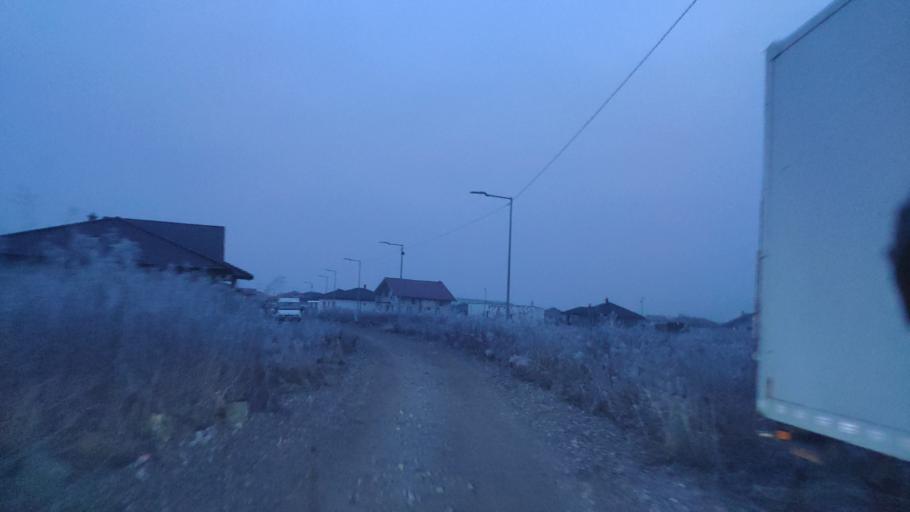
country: SK
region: Kosicky
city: Kosice
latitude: 48.6159
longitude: 21.3327
